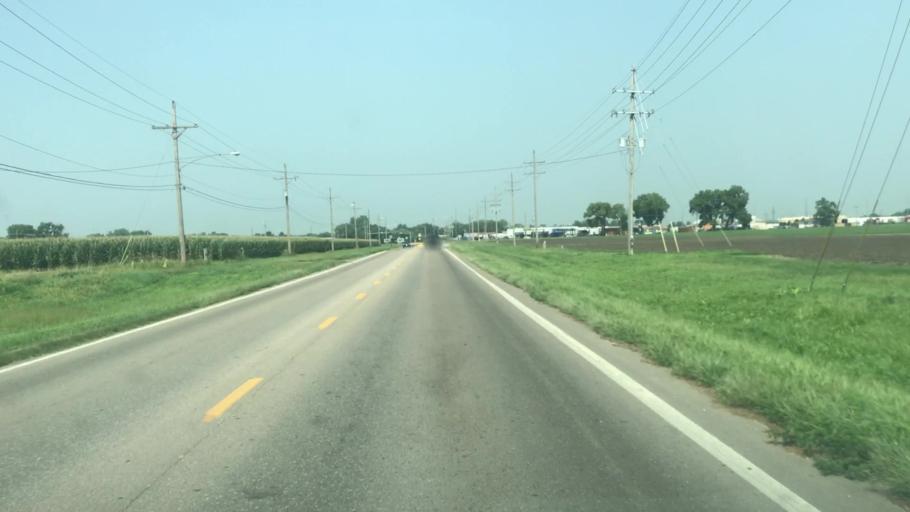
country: US
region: Nebraska
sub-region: Hall County
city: Grand Island
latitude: 40.9271
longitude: -98.3206
